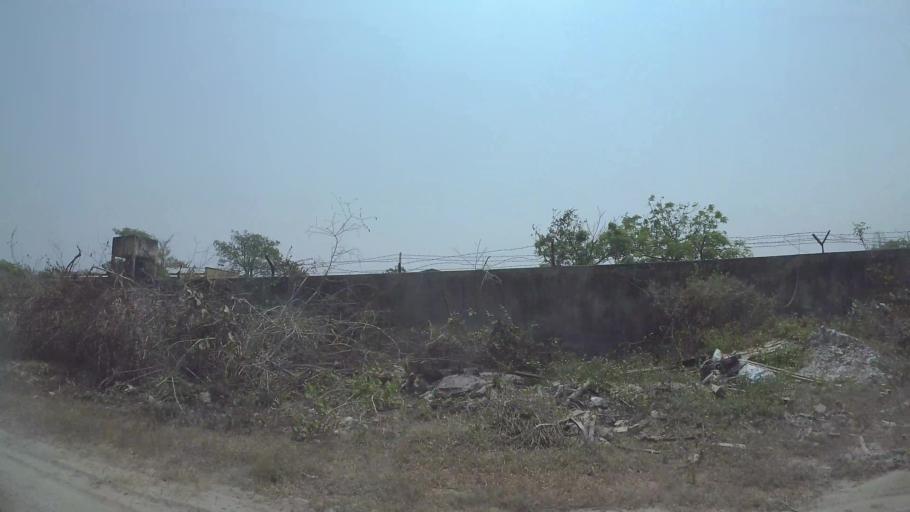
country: VN
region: Da Nang
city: Ngu Hanh Son
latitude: 15.9889
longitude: 108.2532
